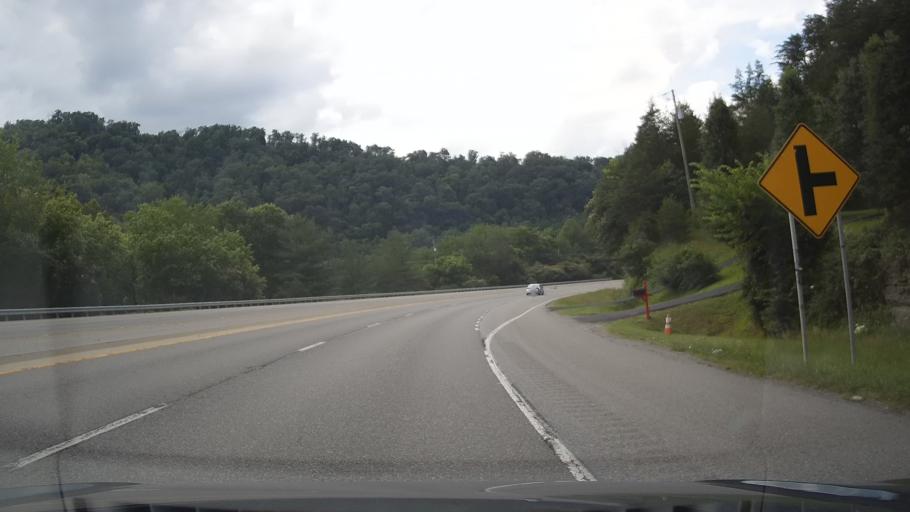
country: US
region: Kentucky
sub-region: Pike County
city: Coal Run Village
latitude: 37.5747
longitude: -82.6595
